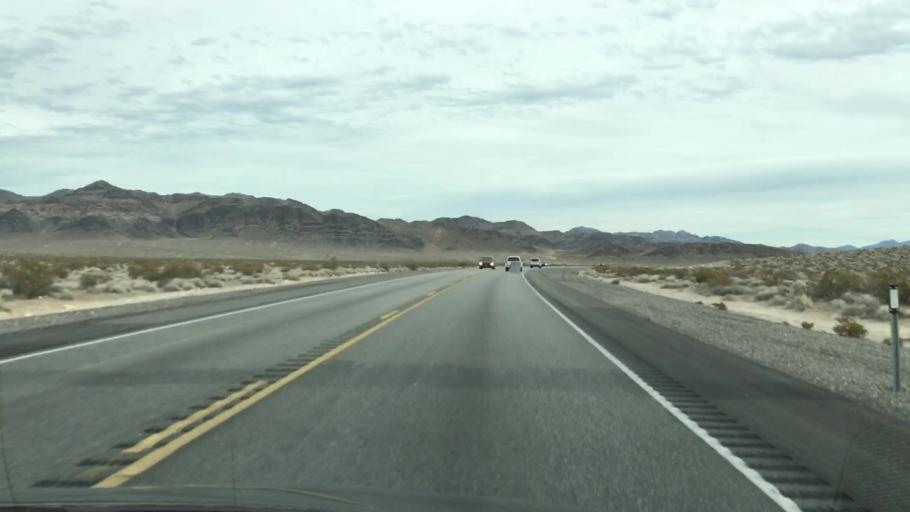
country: US
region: Nevada
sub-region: Nye County
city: Beatty
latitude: 36.6316
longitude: -116.3233
